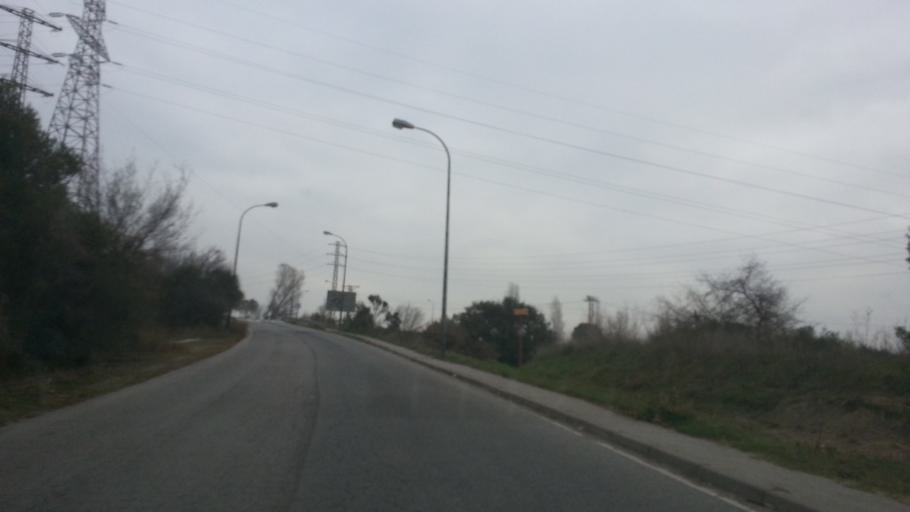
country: ES
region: Catalonia
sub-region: Provincia de Barcelona
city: Barbera del Valles
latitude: 41.4970
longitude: 2.1165
